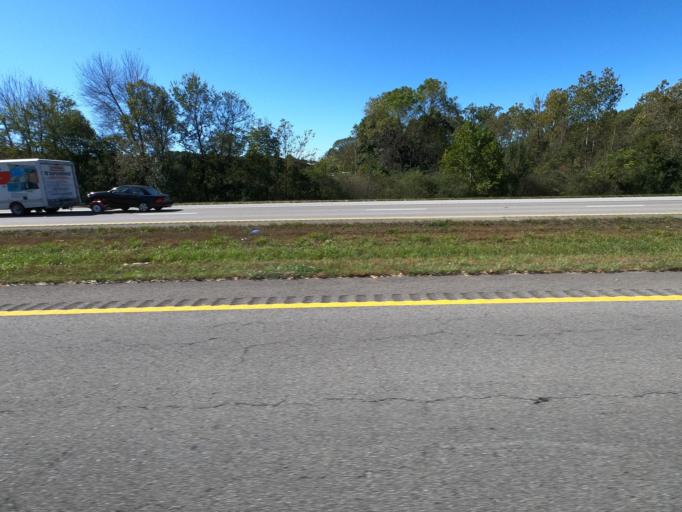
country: US
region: Tennessee
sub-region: Lawrence County
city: Lawrenceburg
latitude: 35.3894
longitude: -87.2762
